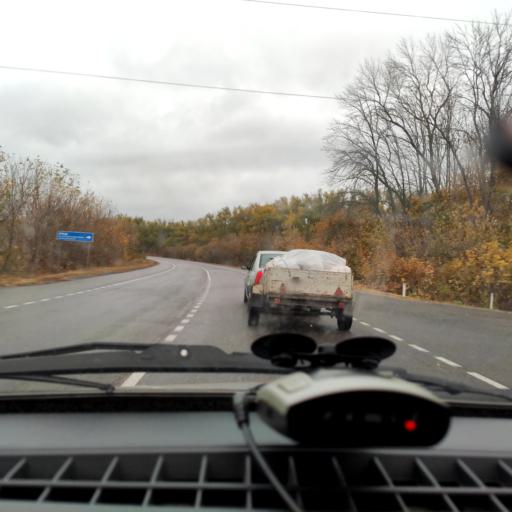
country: RU
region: Voronezj
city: Devitsa
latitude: 51.5929
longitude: 38.9778
